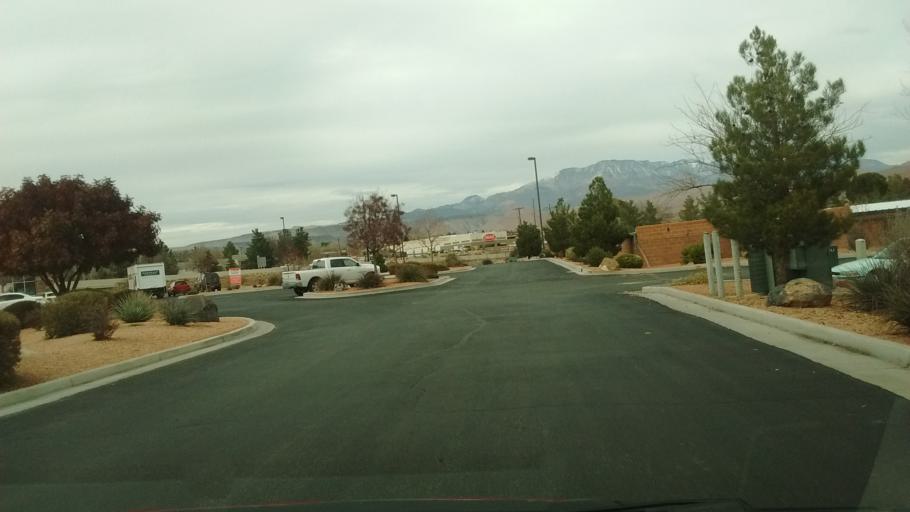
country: US
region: Utah
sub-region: Washington County
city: Washington
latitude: 37.1300
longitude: -113.5198
